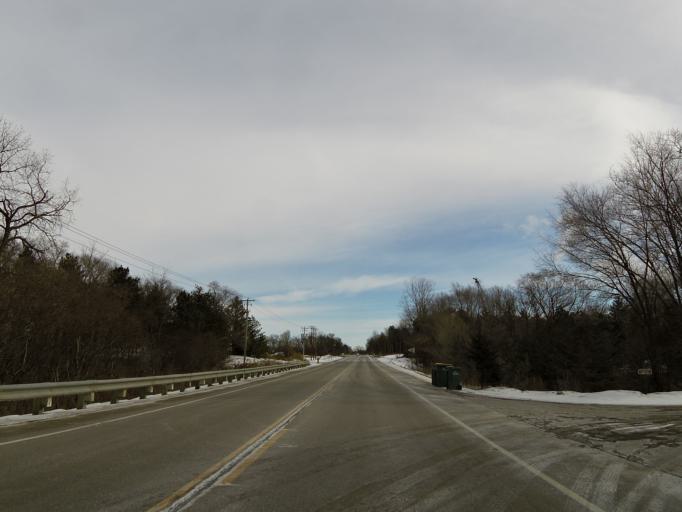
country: US
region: Minnesota
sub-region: Washington County
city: Oak Park Heights
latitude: 45.0487
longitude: -92.7831
